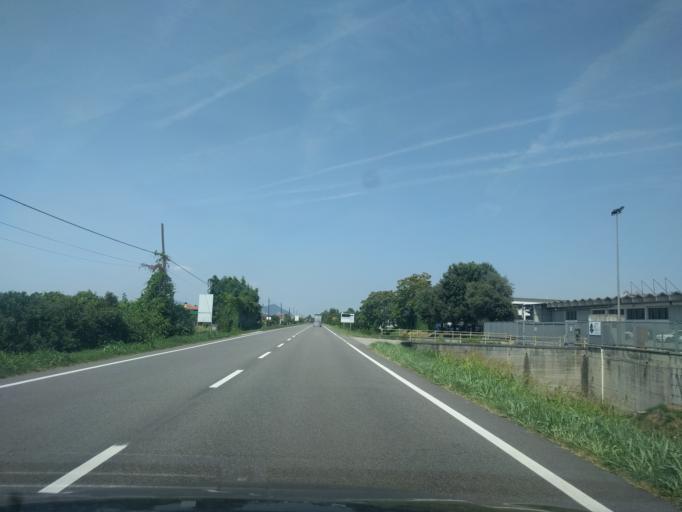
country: IT
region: Veneto
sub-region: Provincia di Padova
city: Stanghella
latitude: 45.1583
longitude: 11.7573
